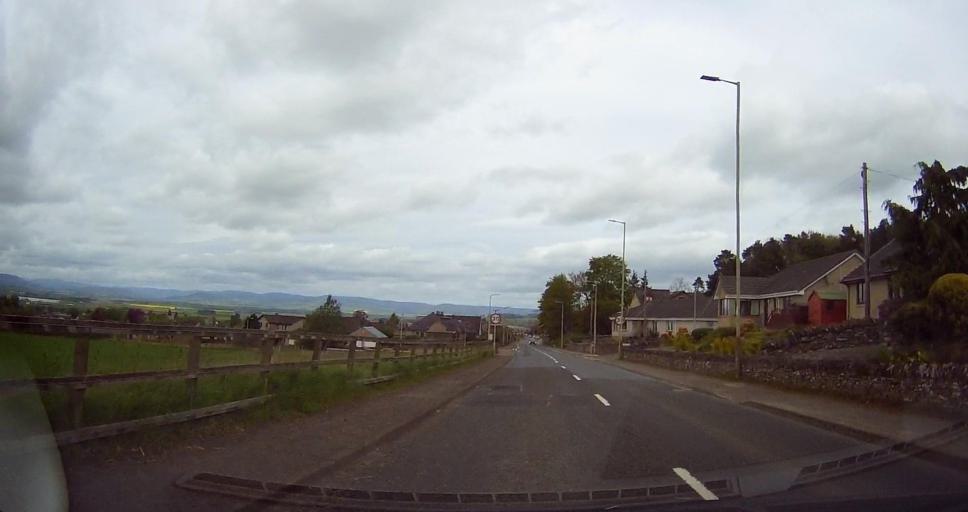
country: GB
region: Scotland
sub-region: Angus
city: Forfar
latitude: 56.6301
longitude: -2.8967
